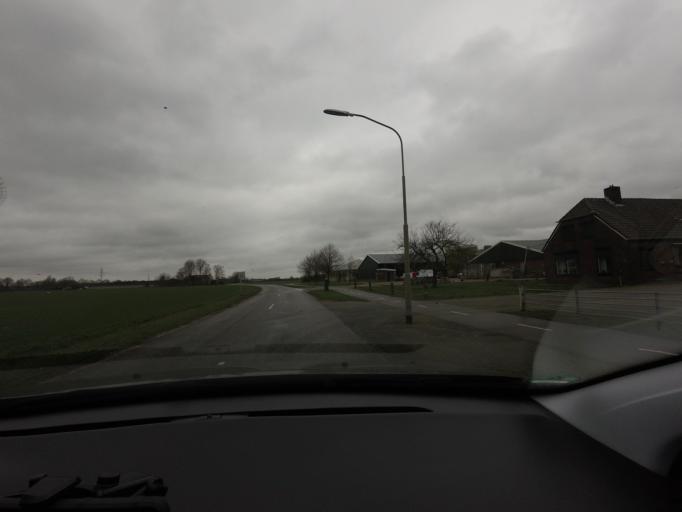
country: NL
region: Drenthe
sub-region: Gemeente Hoogeveen
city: Hoogeveen
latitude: 52.8218
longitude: 6.5174
